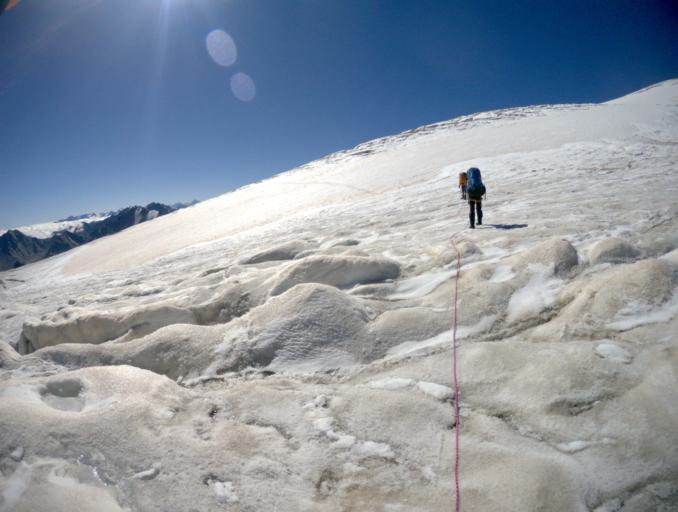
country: RU
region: Kabardino-Balkariya
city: Terskol
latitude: 43.3651
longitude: 42.4962
